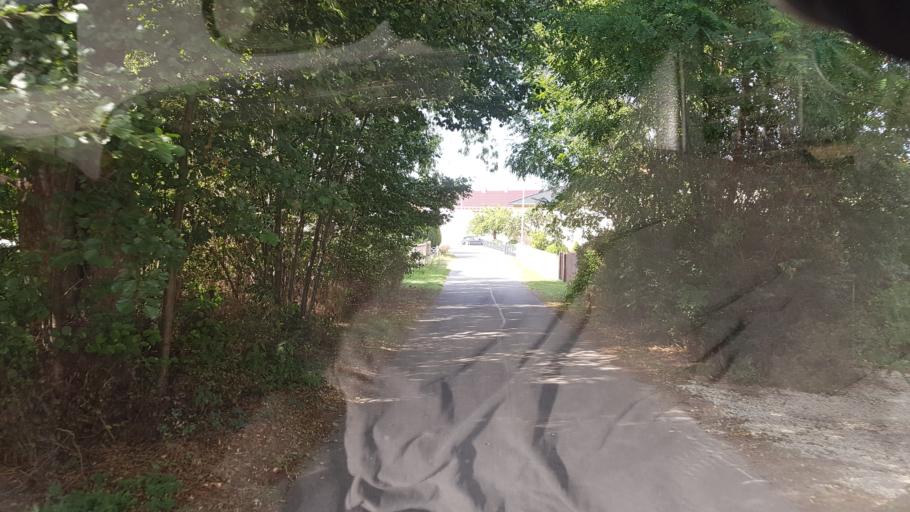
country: DE
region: Brandenburg
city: Hirschfeld
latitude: 51.3844
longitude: 13.6195
